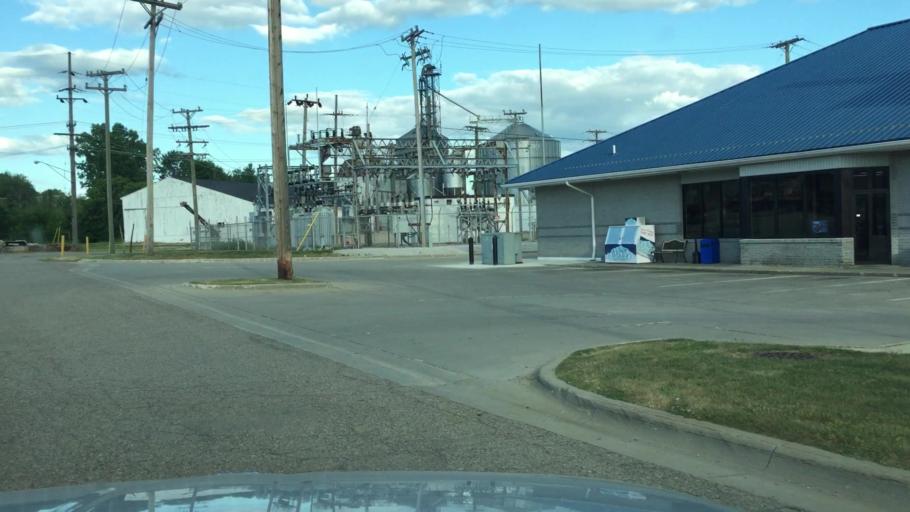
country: US
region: Michigan
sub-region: Saint Clair County
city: Yale
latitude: 43.1318
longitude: -82.7983
